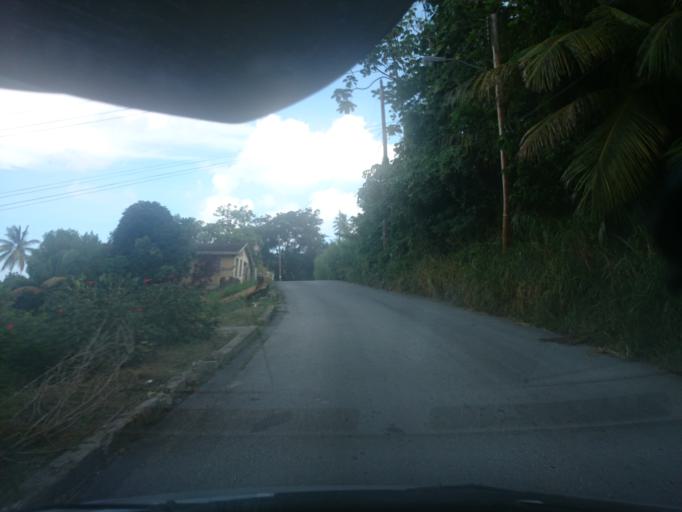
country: BB
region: Saint Joseph
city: Bathsheba
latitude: 13.2062
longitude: -59.5248
